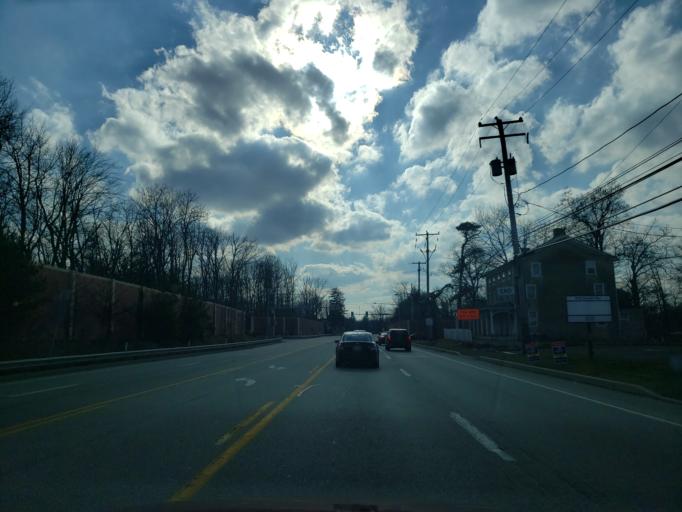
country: US
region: Pennsylvania
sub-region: Montgomery County
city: North Wales
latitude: 40.2134
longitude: -75.2507
